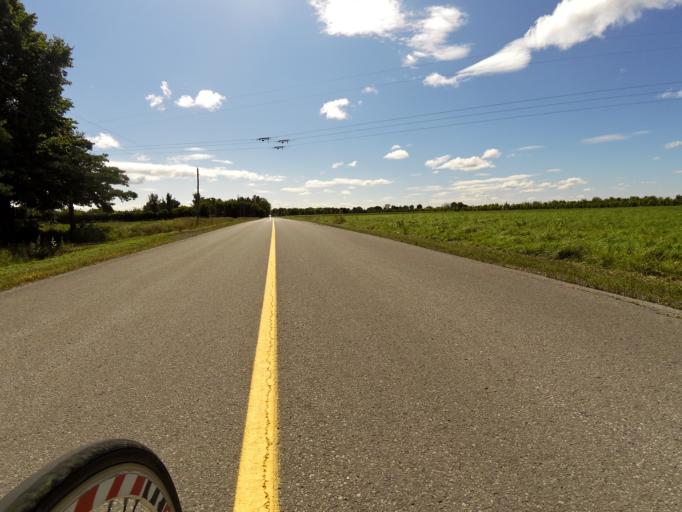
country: CA
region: Ontario
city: Bells Corners
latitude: 45.2475
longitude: -75.8089
